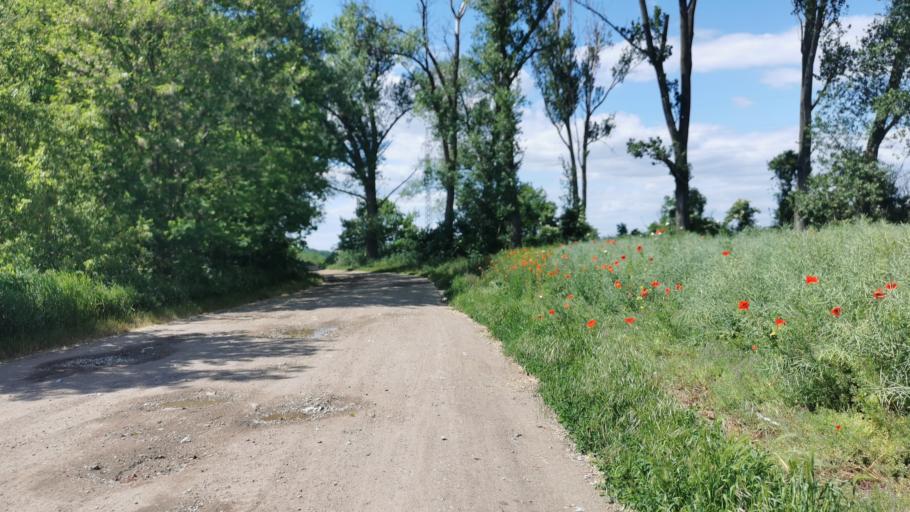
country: SK
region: Trnavsky
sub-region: Okres Skalica
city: Skalica
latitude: 48.8555
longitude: 17.2206
